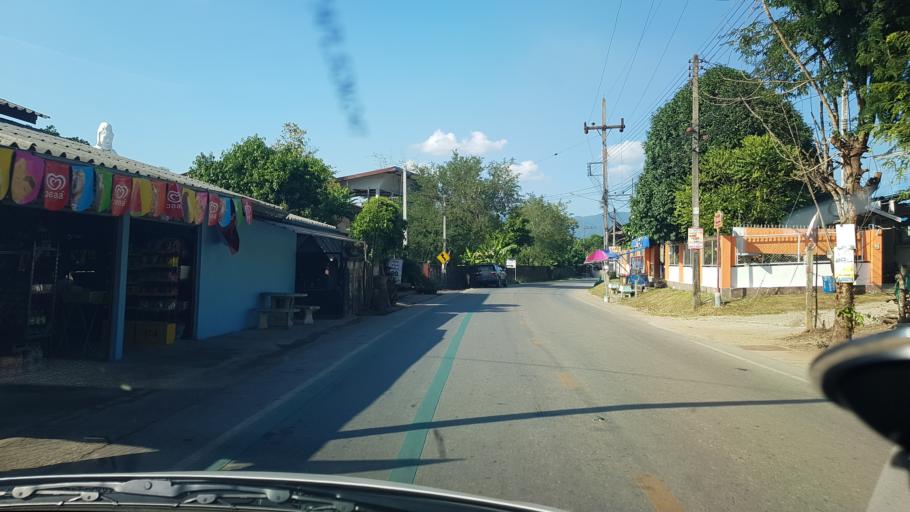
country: TH
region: Chiang Rai
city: Chiang Rai
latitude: 19.9443
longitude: 99.8108
